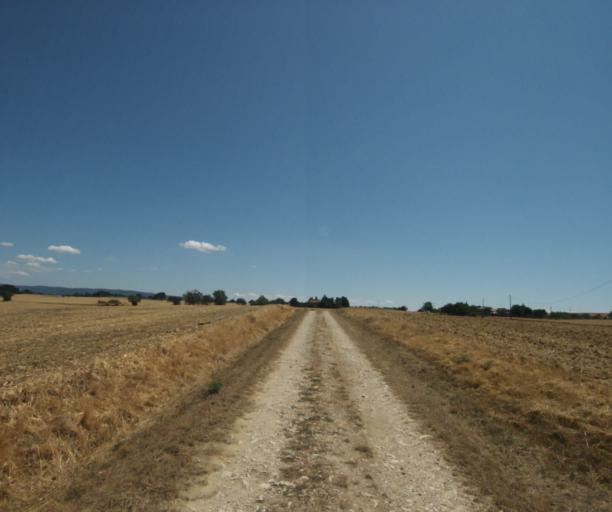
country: FR
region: Midi-Pyrenees
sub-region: Departement de la Haute-Garonne
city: Saint-Felix-Lauragais
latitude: 43.4547
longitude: 1.8976
